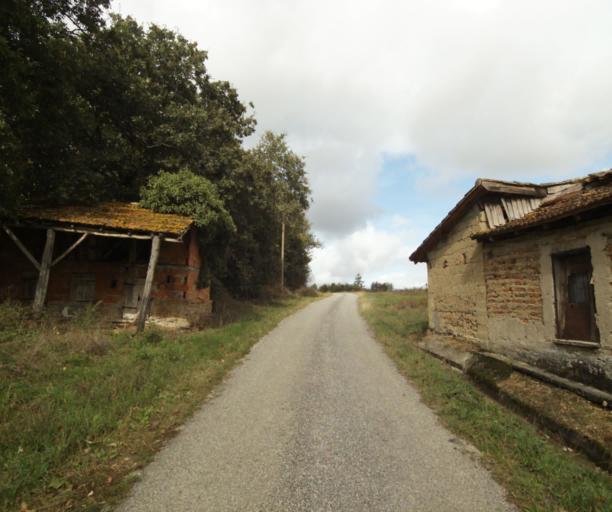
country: FR
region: Midi-Pyrenees
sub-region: Departement du Tarn-et-Garonne
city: Finhan
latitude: 43.8803
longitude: 1.1237
